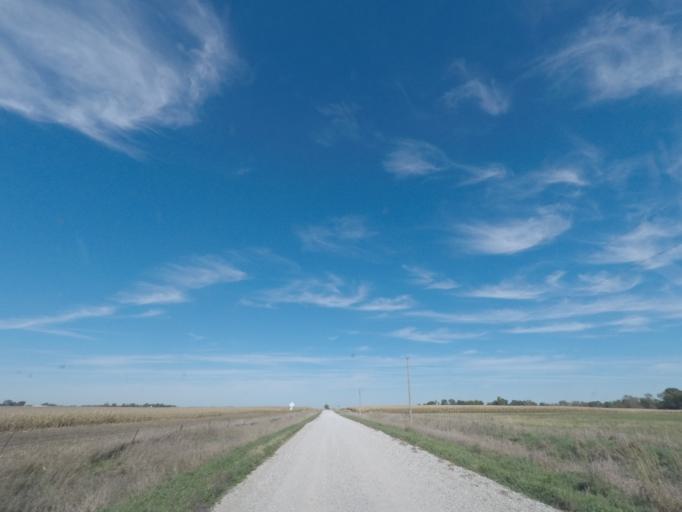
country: US
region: Iowa
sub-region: Story County
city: Nevada
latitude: 42.0136
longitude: -93.3573
